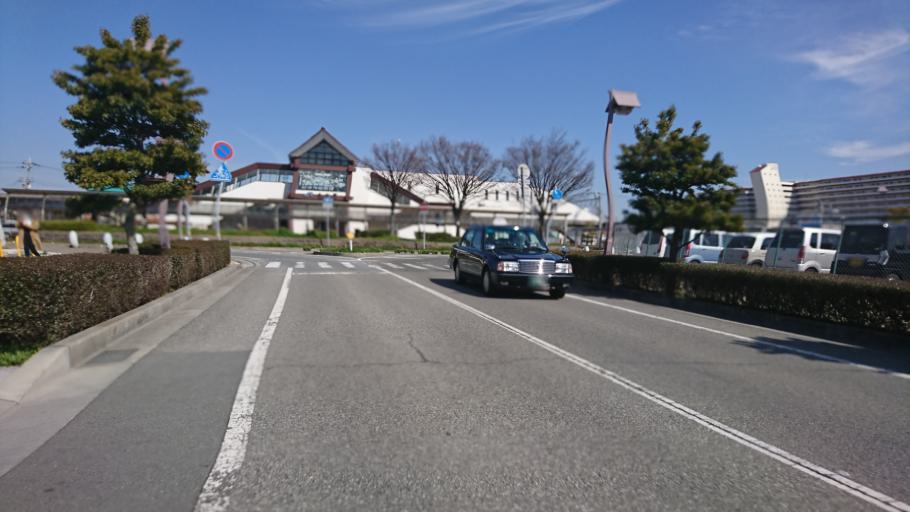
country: JP
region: Hyogo
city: Kakogawacho-honmachi
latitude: 34.7202
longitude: 134.8879
